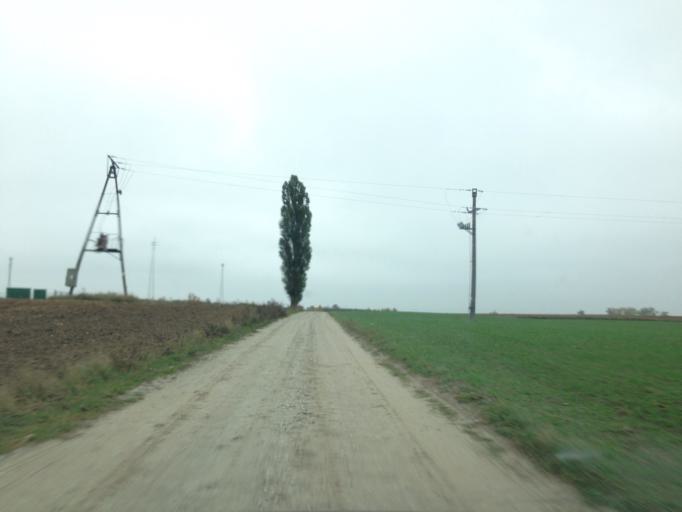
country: PL
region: Kujawsko-Pomorskie
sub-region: Powiat brodnicki
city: Gorzno
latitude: 53.2026
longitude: 19.6255
